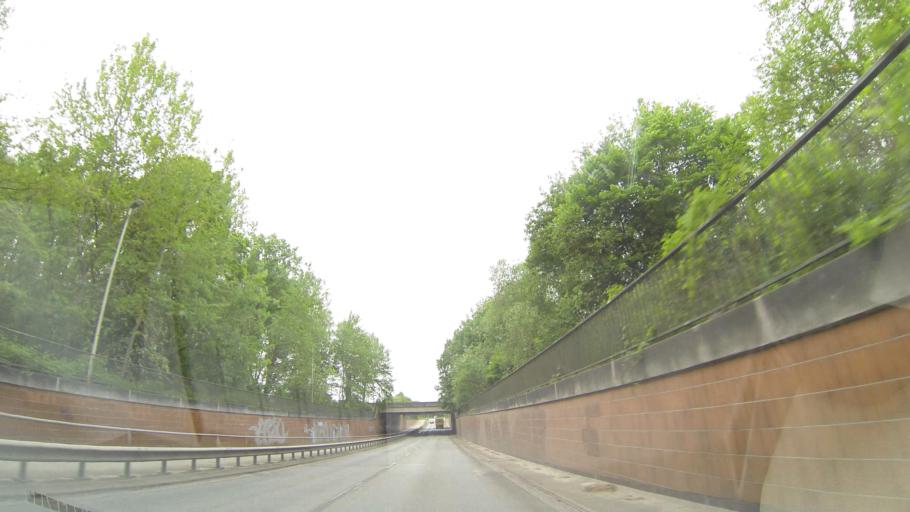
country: DE
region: Schleswig-Holstein
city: Halstenbek
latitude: 53.6210
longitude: 9.8598
